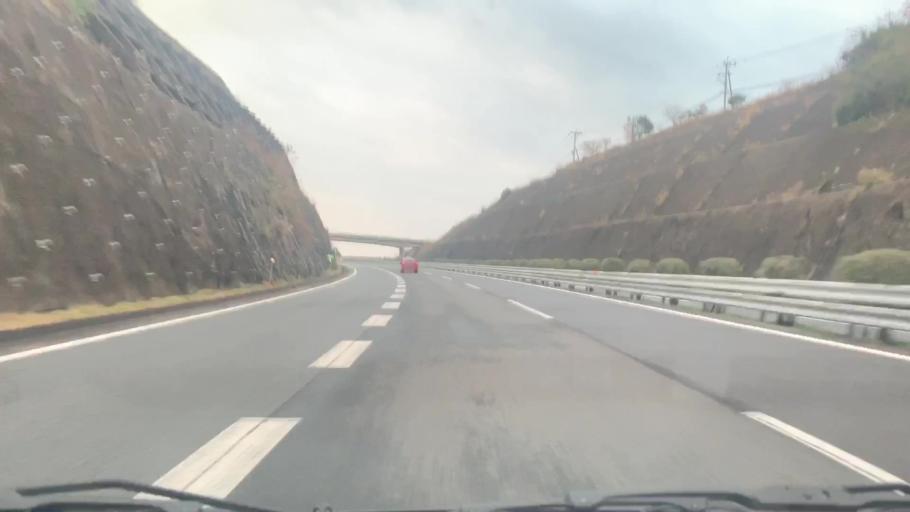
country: JP
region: Nagasaki
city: Omura
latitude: 32.9983
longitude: 129.9510
